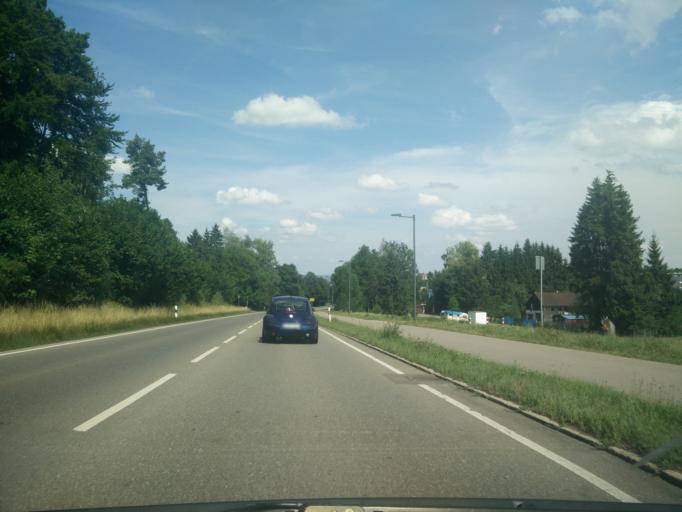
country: DE
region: Baden-Wuerttemberg
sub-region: Freiburg Region
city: Villingen-Schwenningen
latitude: 48.0630
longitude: 8.5058
